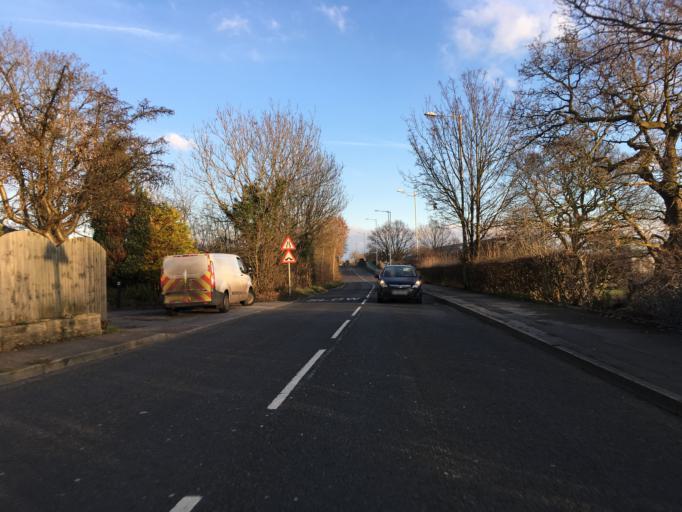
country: GB
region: England
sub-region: Borough of Stockport
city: Cheadle Hulme
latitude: 53.3587
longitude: -2.2078
